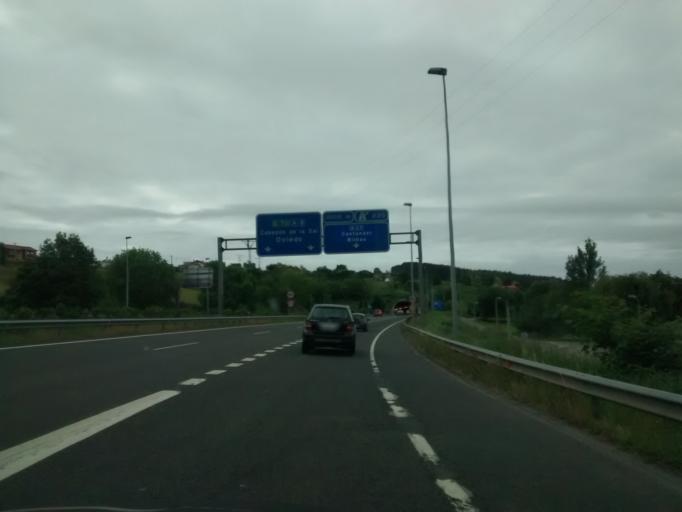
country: ES
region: Cantabria
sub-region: Provincia de Cantabria
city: Torrelavega
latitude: 43.3522
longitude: -4.0366
